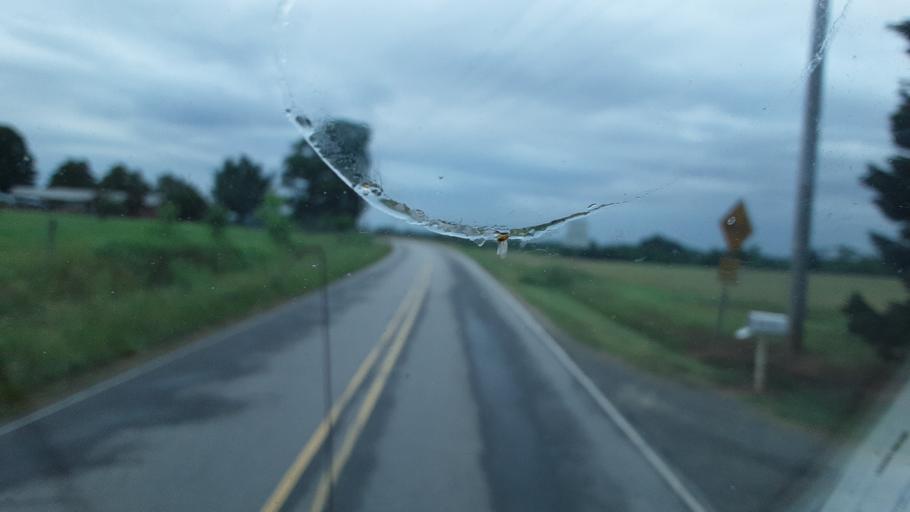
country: US
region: North Carolina
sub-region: Yadkin County
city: Jonesville
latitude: 36.0550
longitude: -80.8312
